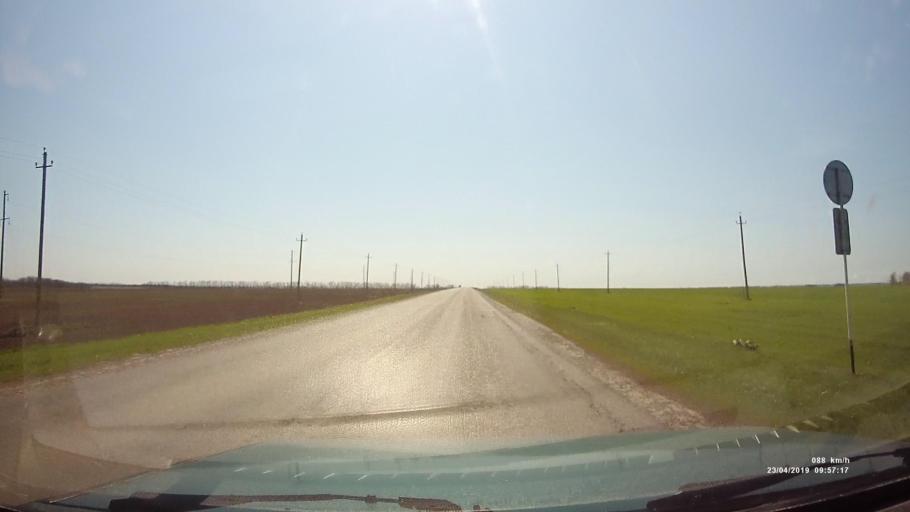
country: RU
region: Rostov
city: Orlovskiy
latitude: 46.7903
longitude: 42.0835
